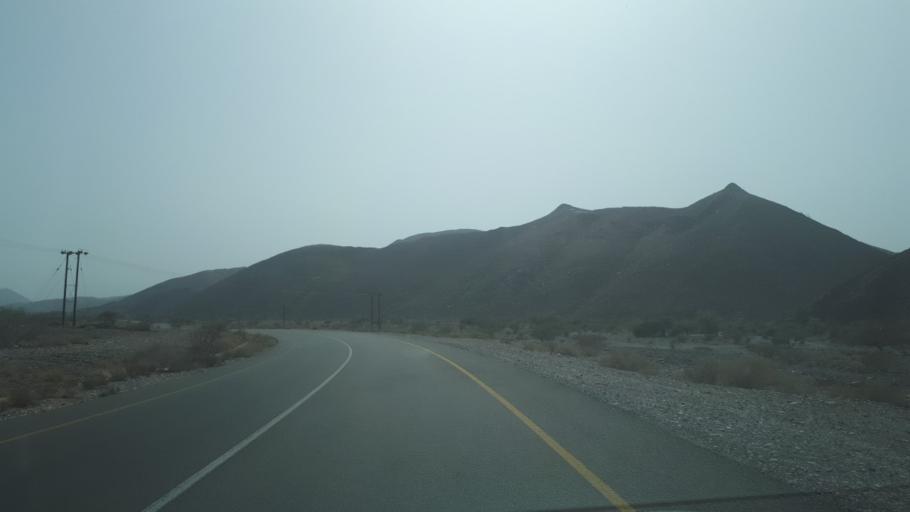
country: OM
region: Muhafazat ad Dakhiliyah
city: Bahla'
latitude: 23.2233
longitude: 56.9812
